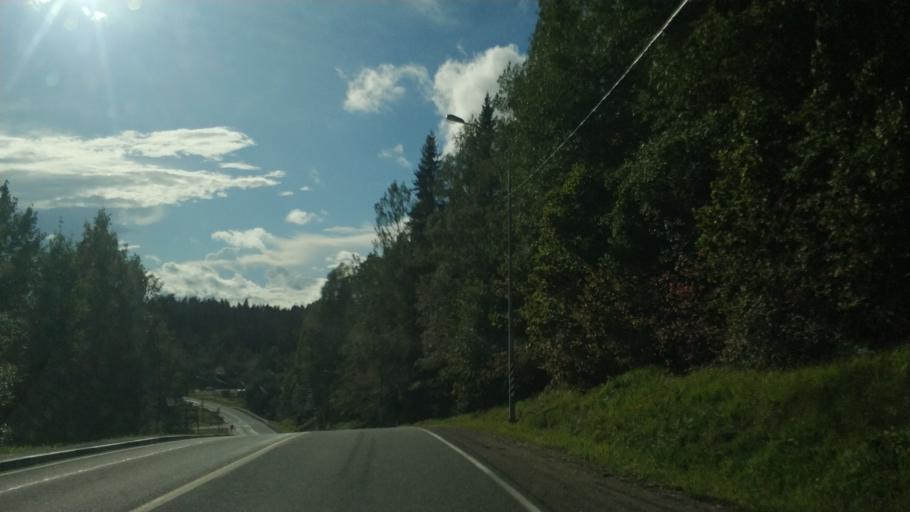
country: RU
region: Republic of Karelia
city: Lakhdenpokh'ya
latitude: 61.5365
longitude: 30.2204
